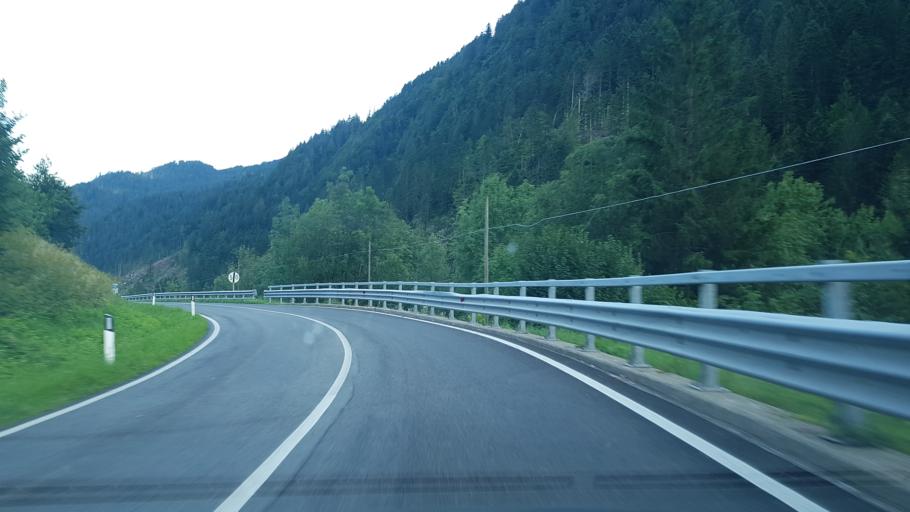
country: IT
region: Friuli Venezia Giulia
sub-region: Provincia di Udine
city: Forni Avoltri
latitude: 46.5826
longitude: 12.7829
